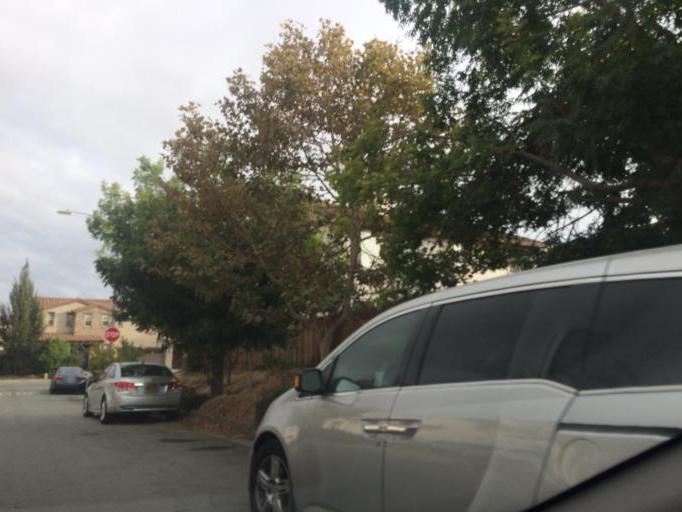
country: US
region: California
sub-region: Santa Clara County
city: Milpitas
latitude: 37.4013
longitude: -121.8801
